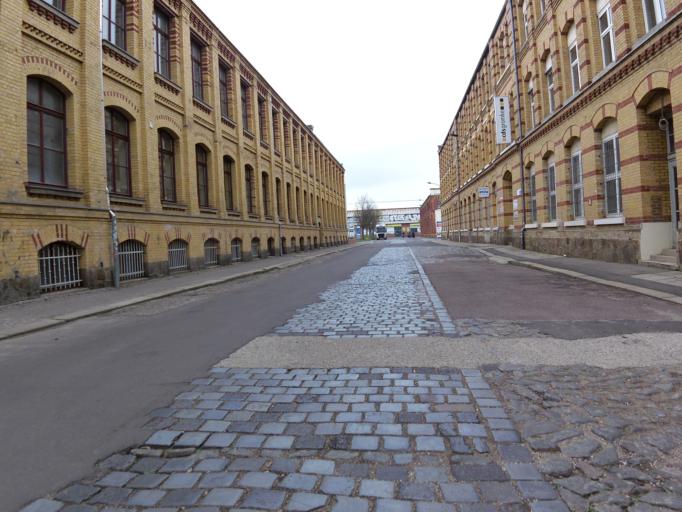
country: DE
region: Saxony
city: Leipzig
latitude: 51.3236
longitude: 12.3298
